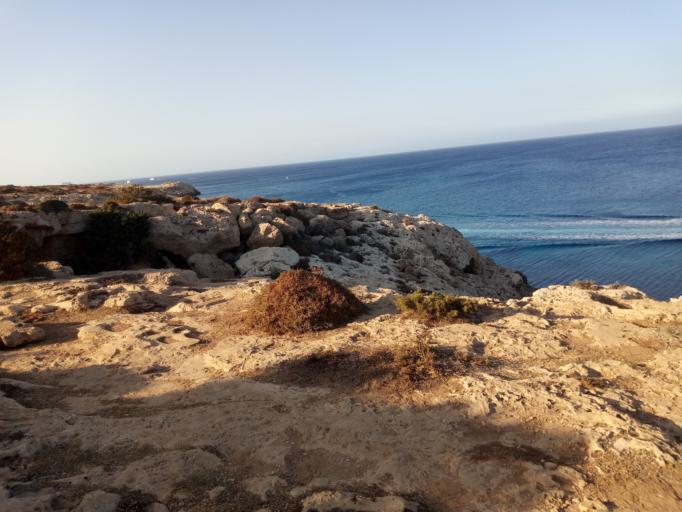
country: CY
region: Ammochostos
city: Protaras
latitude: 34.9703
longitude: 34.0757
